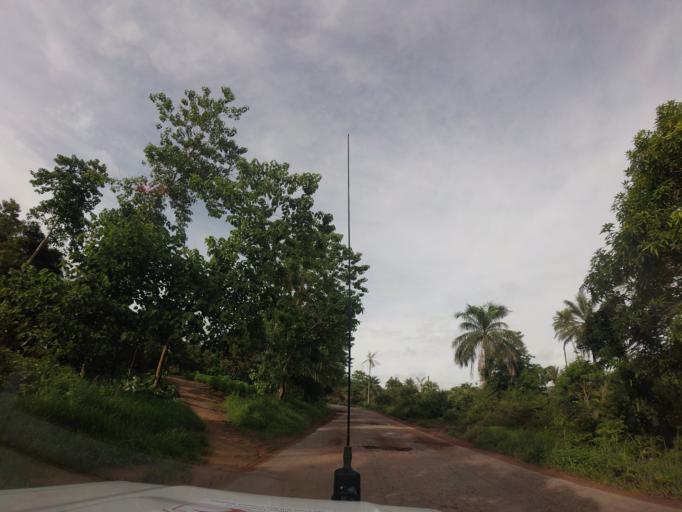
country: GN
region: Kindia
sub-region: Kindia
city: Kindia
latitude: 9.8993
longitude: -13.0466
